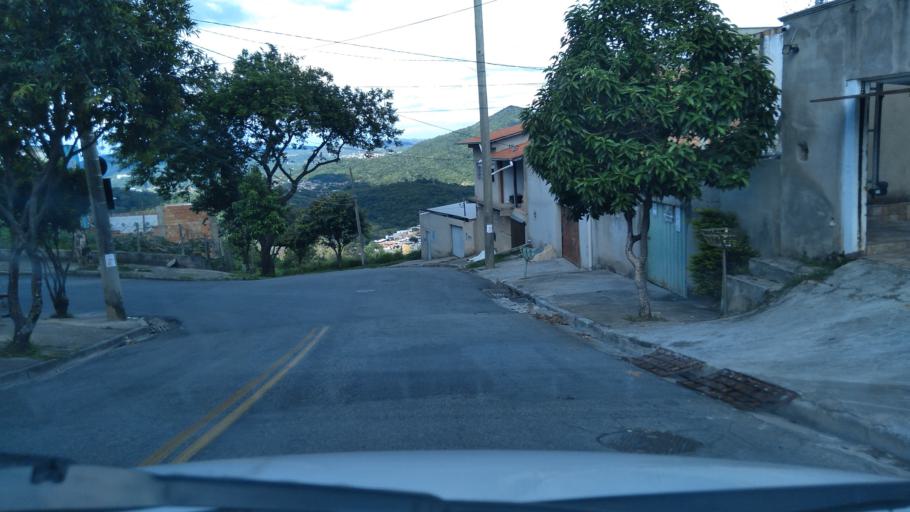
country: BR
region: Minas Gerais
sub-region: Belo Horizonte
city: Belo Horizonte
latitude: -19.8603
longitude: -43.8813
